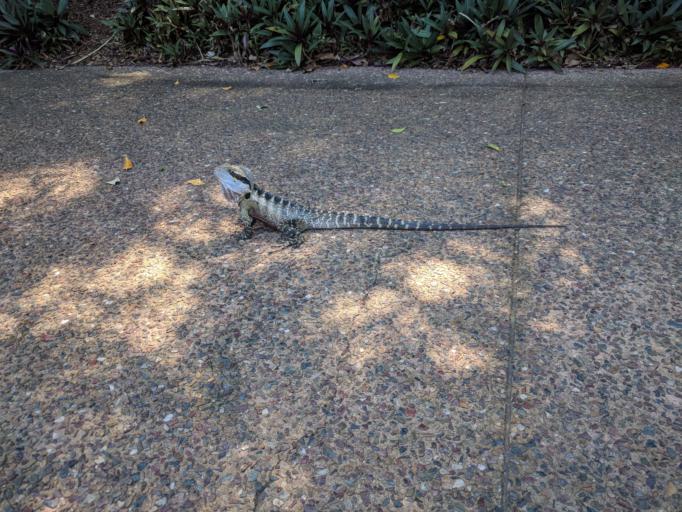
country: AU
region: Queensland
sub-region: Brisbane
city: Spring Hill
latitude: -27.4625
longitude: 153.0191
